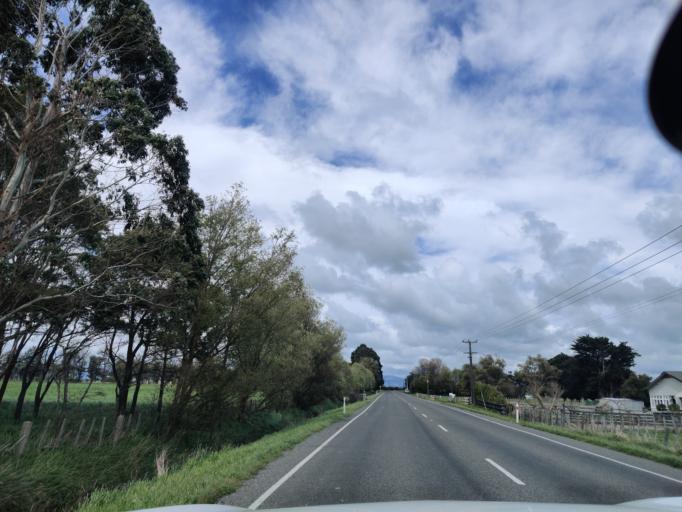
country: NZ
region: Manawatu-Wanganui
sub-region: Palmerston North City
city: Palmerston North
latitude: -40.3252
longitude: 175.5046
